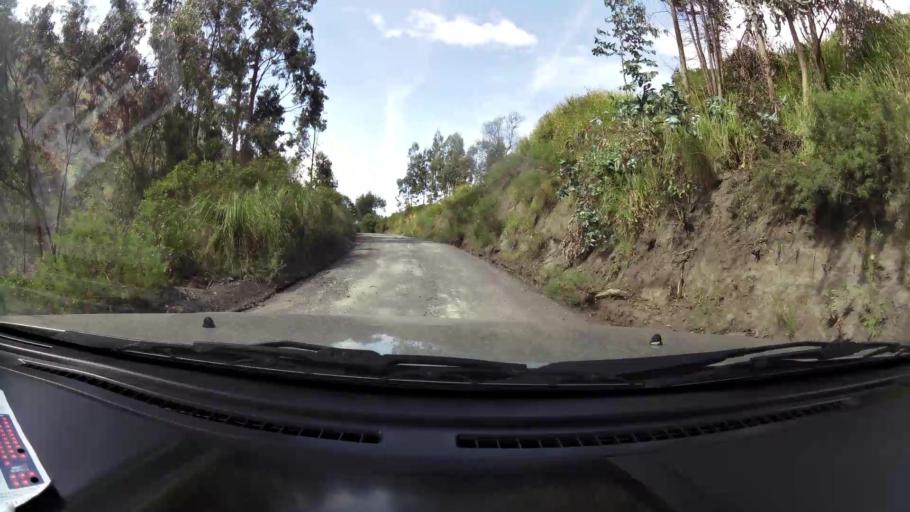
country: EC
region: Tungurahua
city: Banos
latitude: -1.4856
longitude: -78.5117
